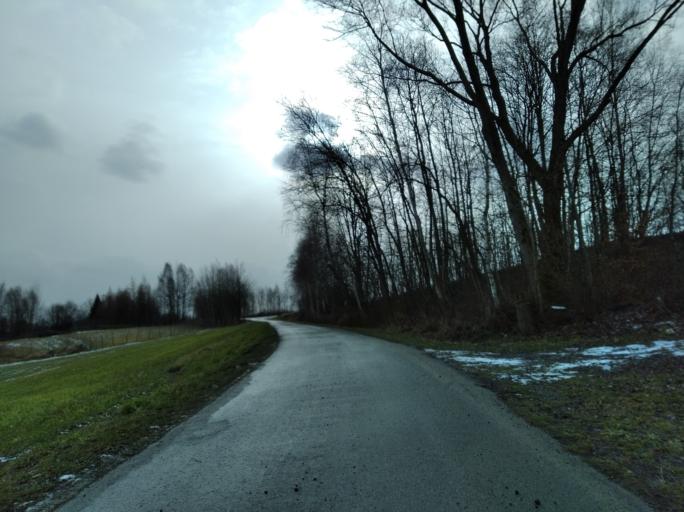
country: PL
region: Subcarpathian Voivodeship
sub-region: Powiat strzyzowski
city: Wysoka Strzyzowska
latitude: 49.8941
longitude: 21.7265
